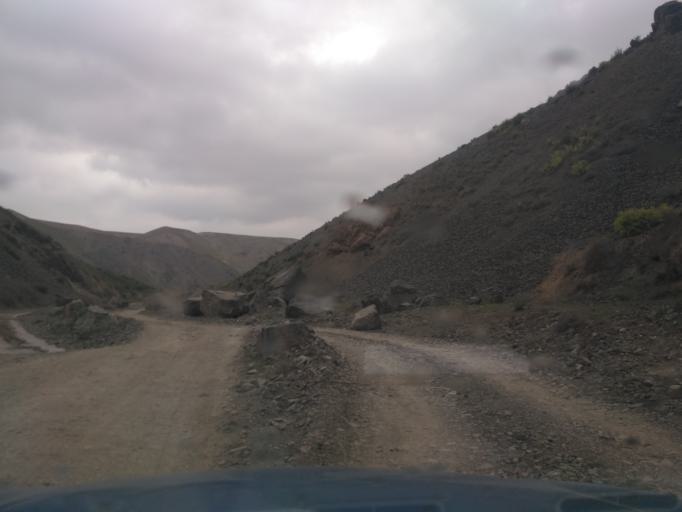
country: UZ
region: Jizzax
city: Zomin
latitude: 39.8605
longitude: 68.3845
